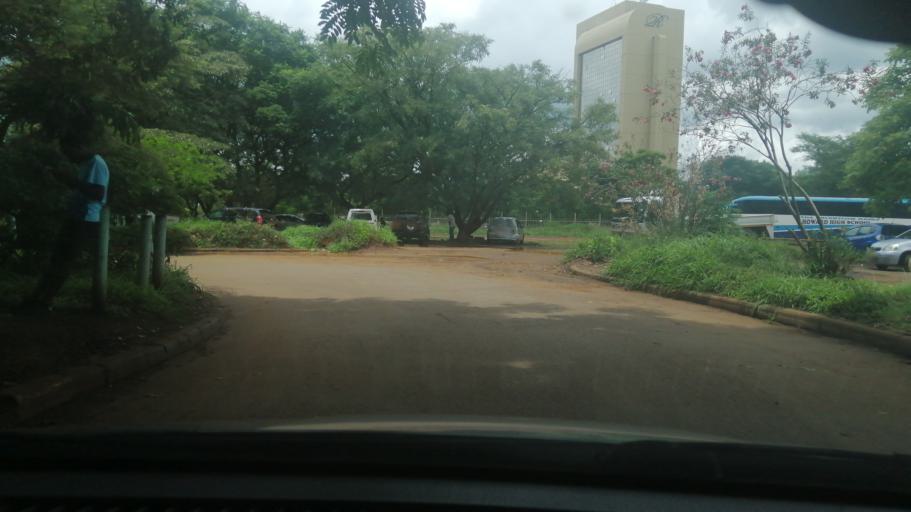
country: ZW
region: Harare
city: Harare
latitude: -17.8327
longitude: 31.0377
